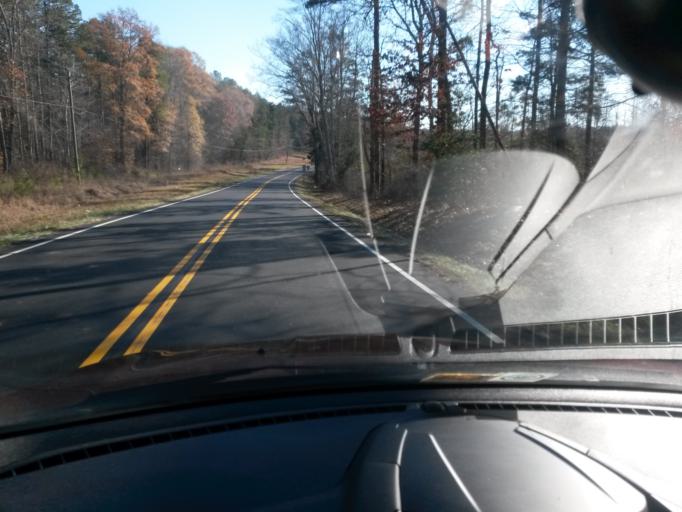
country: US
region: Virginia
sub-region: Charlotte County
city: Charlotte Court House
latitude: 37.0594
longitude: -78.5890
